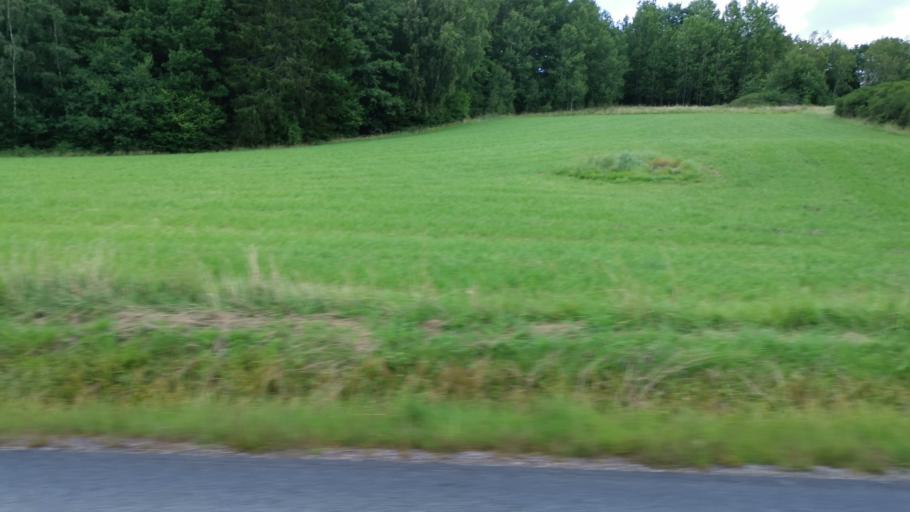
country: SE
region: Vaestra Goetaland
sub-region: Lysekils Kommun
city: Brastad
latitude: 58.4666
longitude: 11.4437
